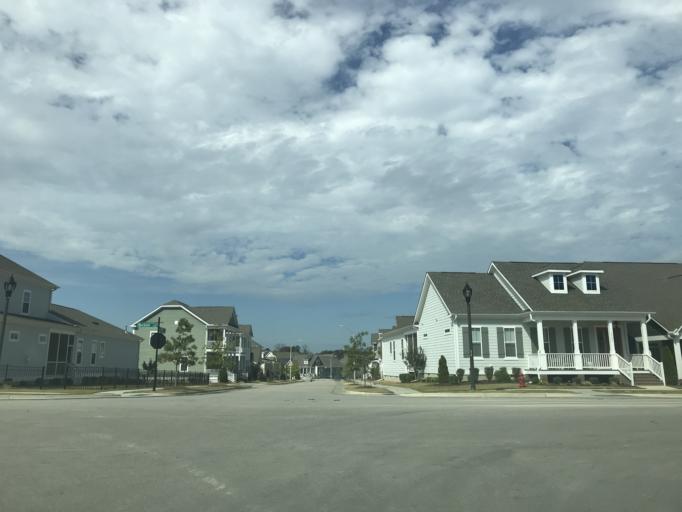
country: US
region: North Carolina
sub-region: Wake County
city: Knightdale
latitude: 35.8602
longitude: -78.5373
